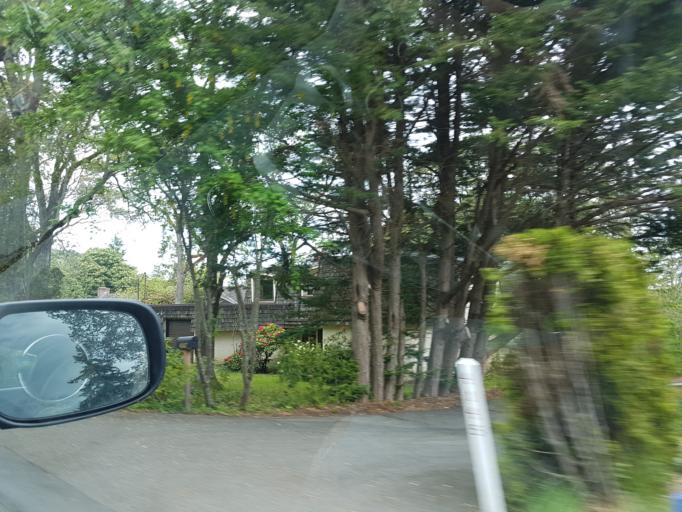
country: CA
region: British Columbia
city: Oak Bay
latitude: 48.4788
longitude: -123.3393
